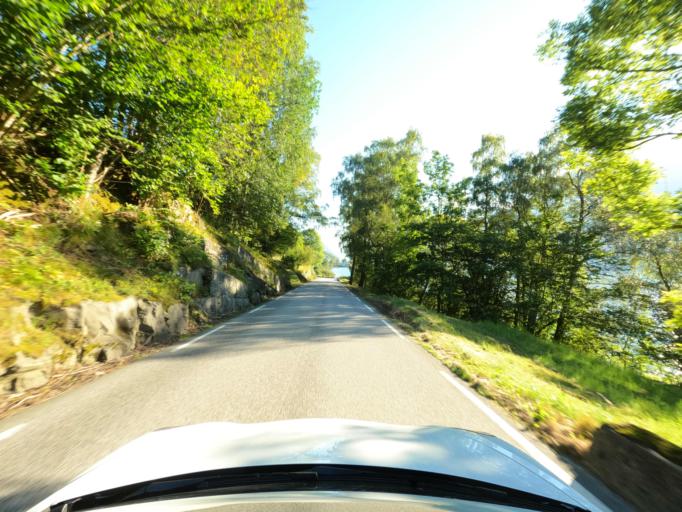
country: NO
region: Hordaland
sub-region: Ullensvang
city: Kinsarvik
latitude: 60.3502
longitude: 6.6613
